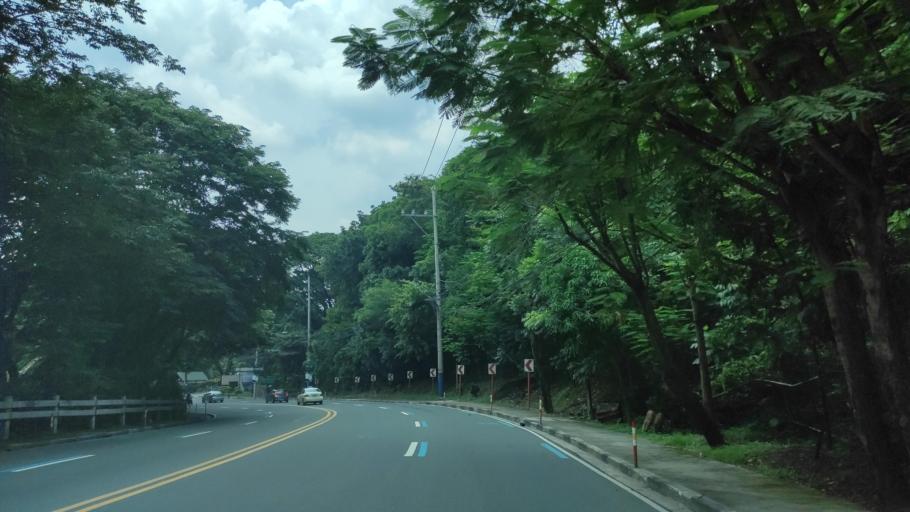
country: PH
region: Calabarzon
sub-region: Province of Rizal
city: Antipolo
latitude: 14.6160
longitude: 121.1521
